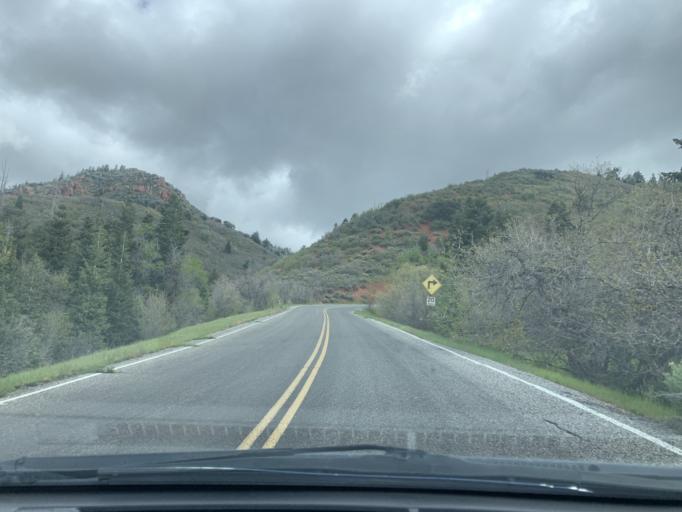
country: US
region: Utah
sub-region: Sanpete County
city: Fountain Green
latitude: 39.7894
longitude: -111.6879
